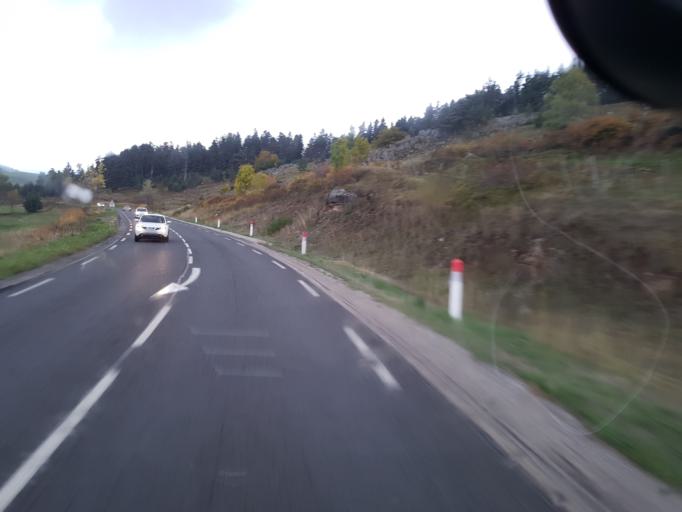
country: FR
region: Languedoc-Roussillon
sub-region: Departement de la Lozere
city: Mende
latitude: 44.5603
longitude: 3.6215
